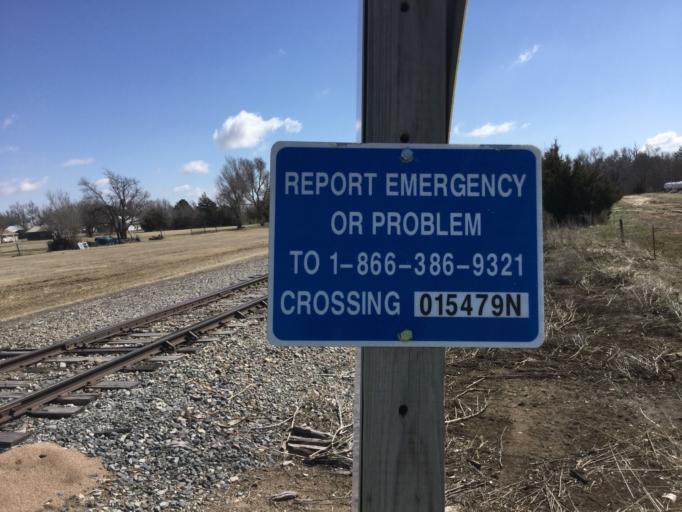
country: US
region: Kansas
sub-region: Barber County
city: Medicine Lodge
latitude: 37.4679
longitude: -98.5560
